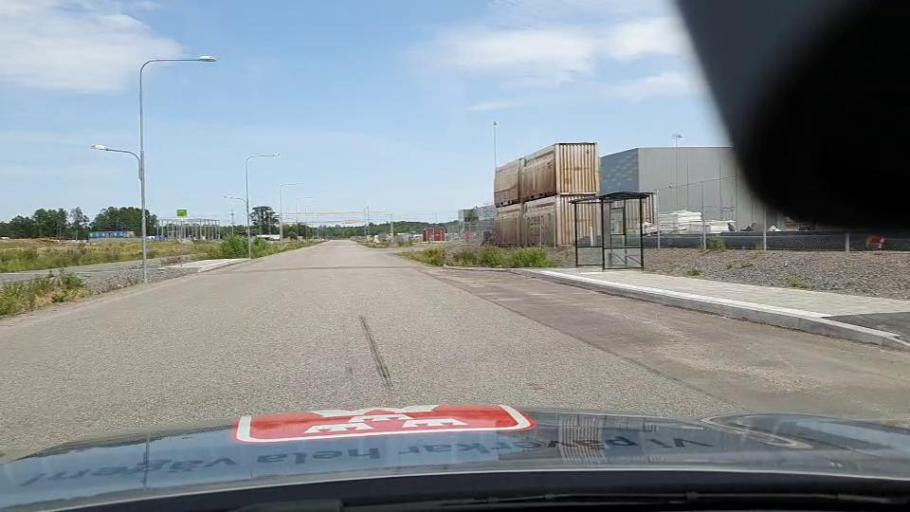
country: SE
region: Soedermanland
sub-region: Eskilstuna Kommun
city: Arla
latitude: 59.3418
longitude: 16.6947
